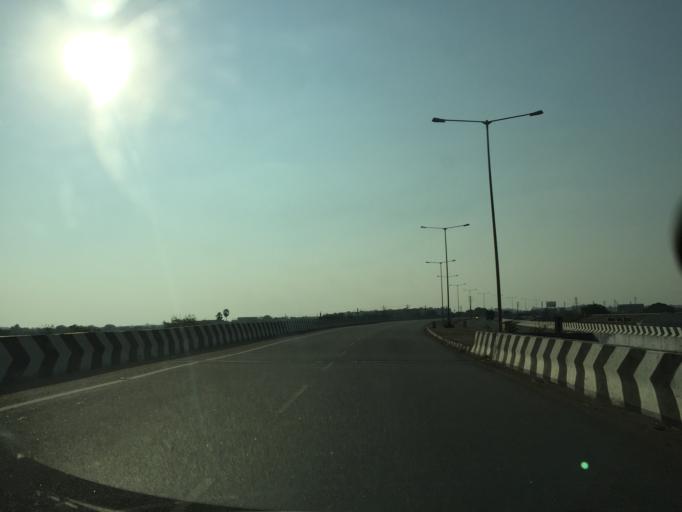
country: IN
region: Telangana
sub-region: Nalgonda
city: Bhongir
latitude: 17.4999
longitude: 78.8906
